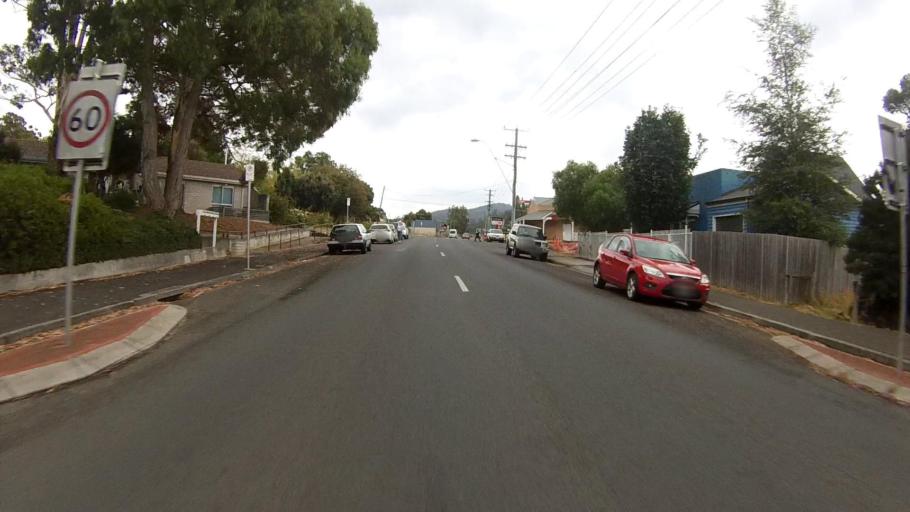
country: AU
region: Tasmania
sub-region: Huon Valley
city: Cygnet
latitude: -43.1592
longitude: 147.0753
